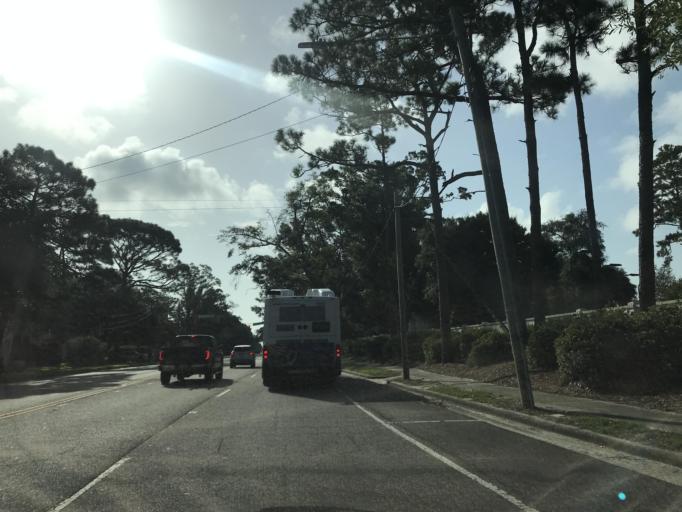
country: US
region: North Carolina
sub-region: New Hanover County
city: Wilmington
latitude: 34.2217
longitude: -77.9165
